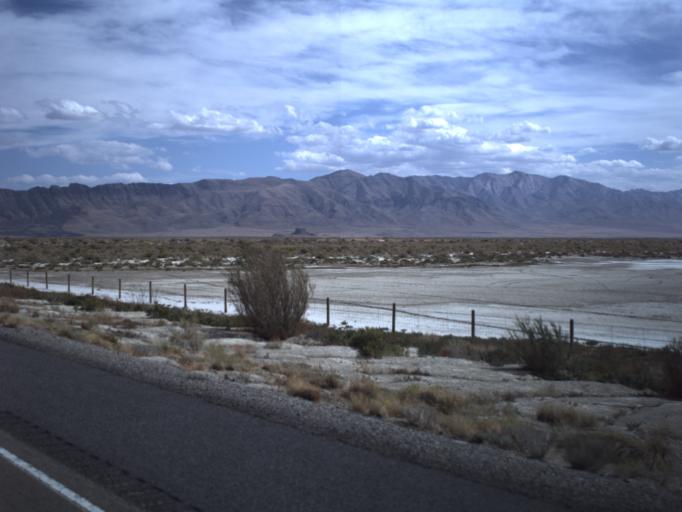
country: US
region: Utah
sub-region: Tooele County
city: Grantsville
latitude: 40.7554
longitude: -112.7510
